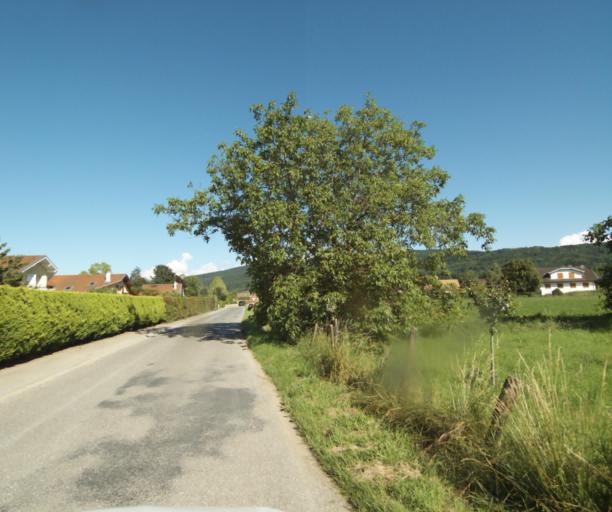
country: FR
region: Rhone-Alpes
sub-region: Departement de la Haute-Savoie
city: Massongy
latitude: 46.3218
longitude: 6.3237
